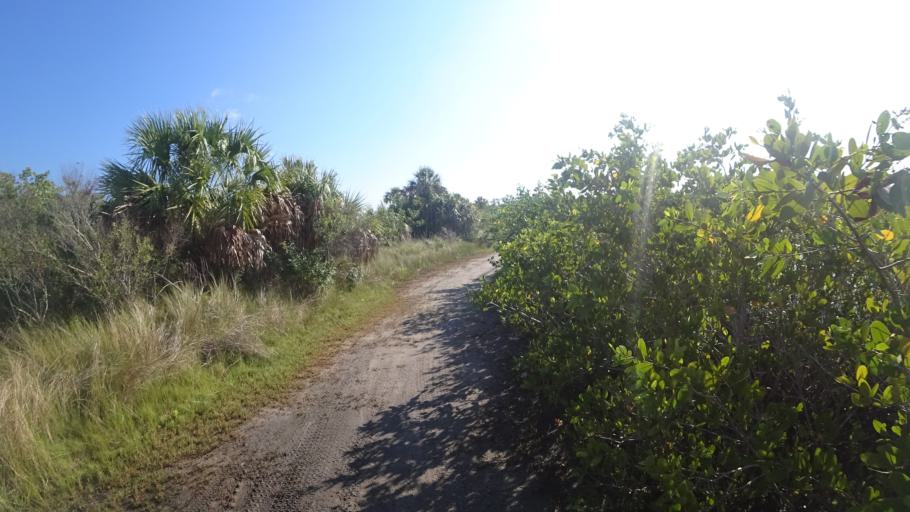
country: US
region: Florida
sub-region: Manatee County
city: Ellenton
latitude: 27.5022
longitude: -82.4890
